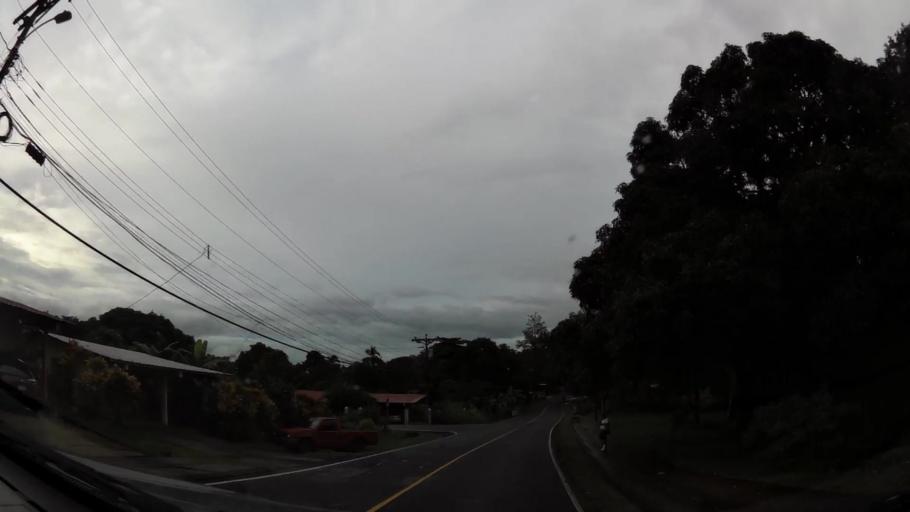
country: PA
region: Veraguas
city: Santiago de Veraguas
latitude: 8.1047
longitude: -80.9823
